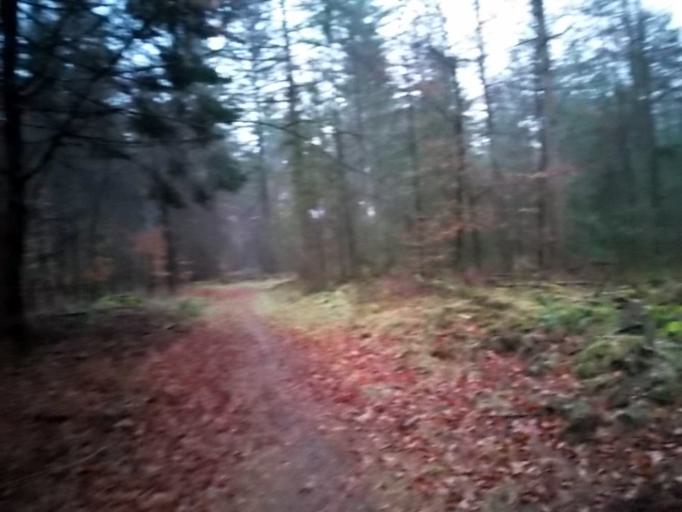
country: NL
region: Gelderland
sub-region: Gemeente Barneveld
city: Garderen
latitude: 52.2357
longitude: 5.6790
